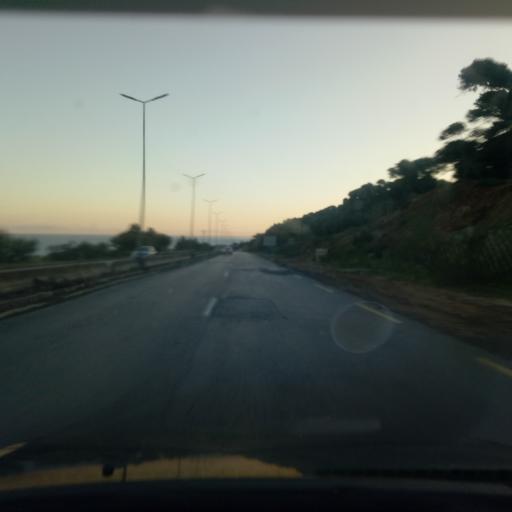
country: DZ
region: Tipaza
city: Bou Ismail
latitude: 36.6527
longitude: 2.7160
